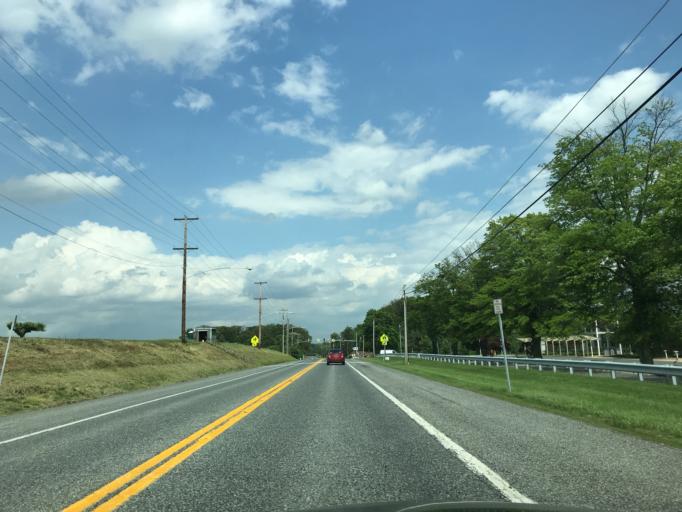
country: US
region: Pennsylvania
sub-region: York County
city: Susquehanna Trails
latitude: 39.6763
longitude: -76.4019
